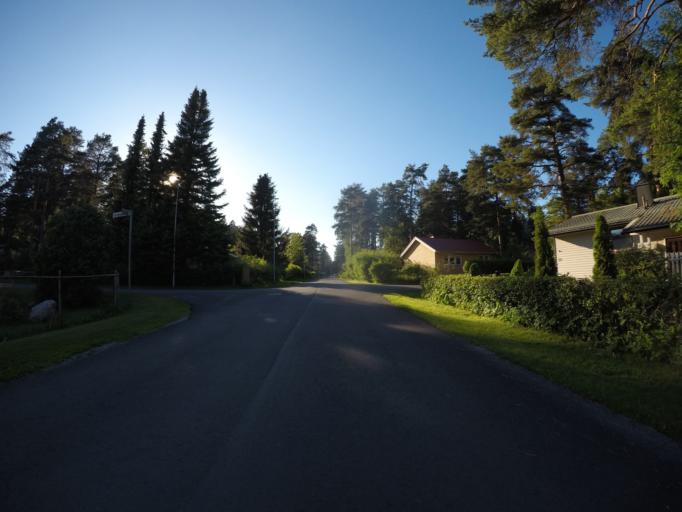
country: FI
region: Haeme
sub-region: Haemeenlinna
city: Haemeenlinna
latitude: 60.9806
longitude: 24.4623
